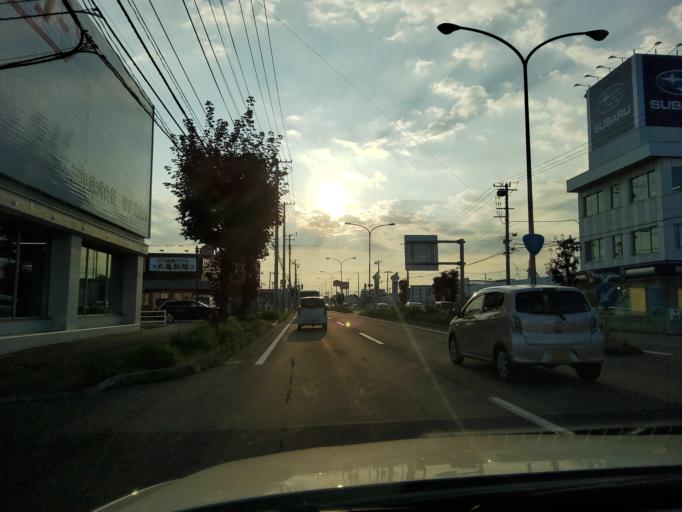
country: JP
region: Hokkaido
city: Obihiro
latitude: 42.9309
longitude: 143.1823
